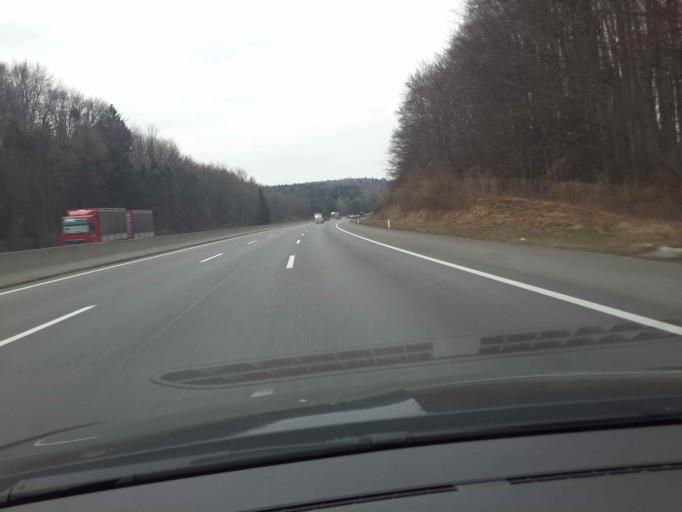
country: AT
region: Lower Austria
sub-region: Politischer Bezirk Baden
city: Klausen-Leopoldsdorf
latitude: 48.1150
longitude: 15.9730
